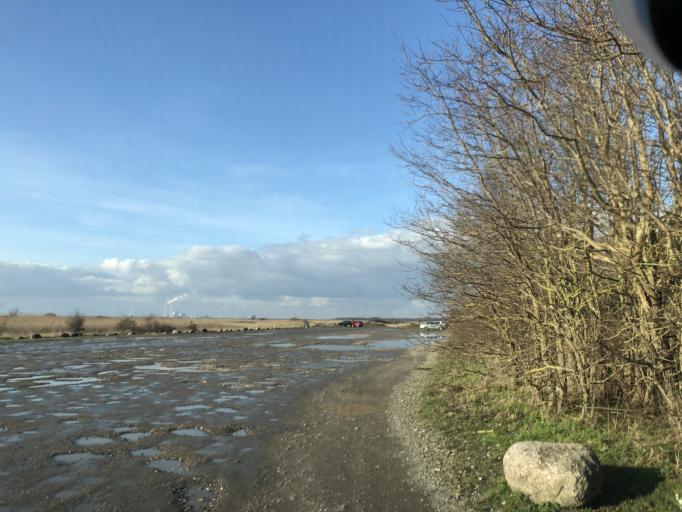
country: DK
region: Capital Region
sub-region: Tarnby Kommune
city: Tarnby
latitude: 55.5633
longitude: 12.5637
